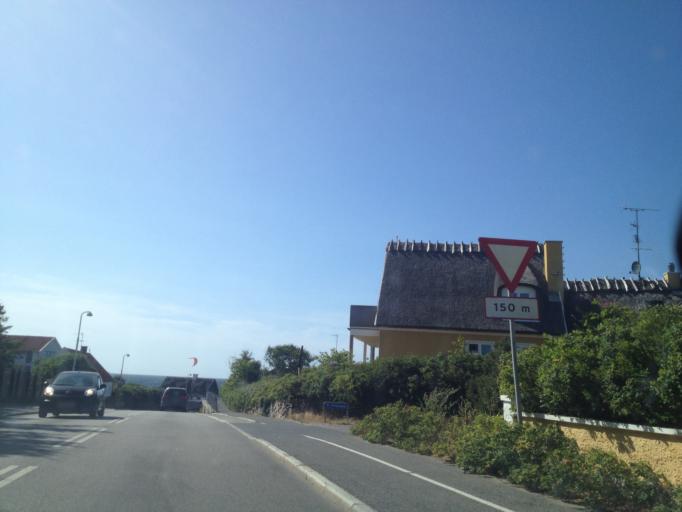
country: DK
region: Capital Region
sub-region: Gribskov Kommune
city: Helsinge
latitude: 56.0987
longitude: 12.1646
